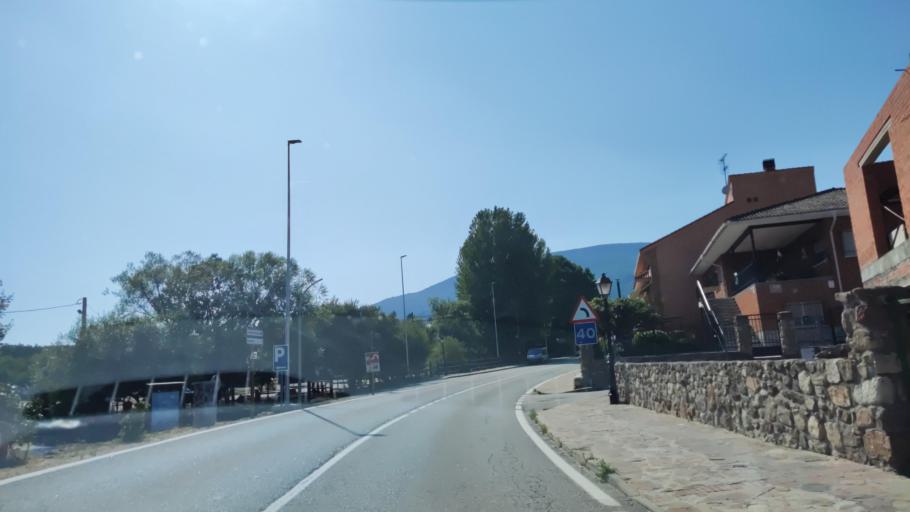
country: ES
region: Madrid
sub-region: Provincia de Madrid
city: Lozoya
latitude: 40.9491
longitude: -3.7899
